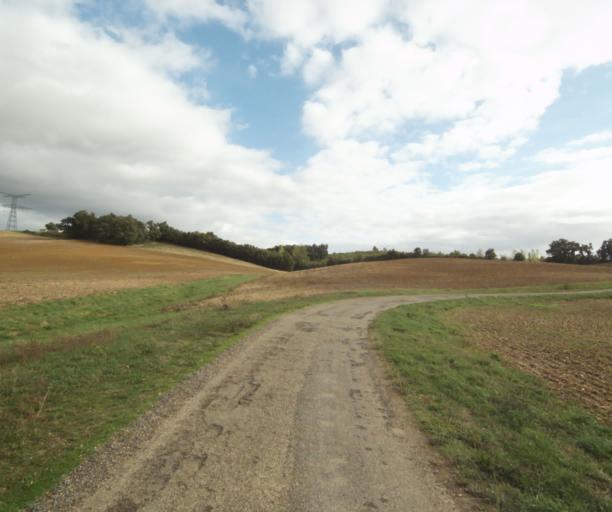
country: FR
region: Midi-Pyrenees
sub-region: Departement du Tarn-et-Garonne
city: Beaumont-de-Lomagne
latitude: 43.9111
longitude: 1.0953
